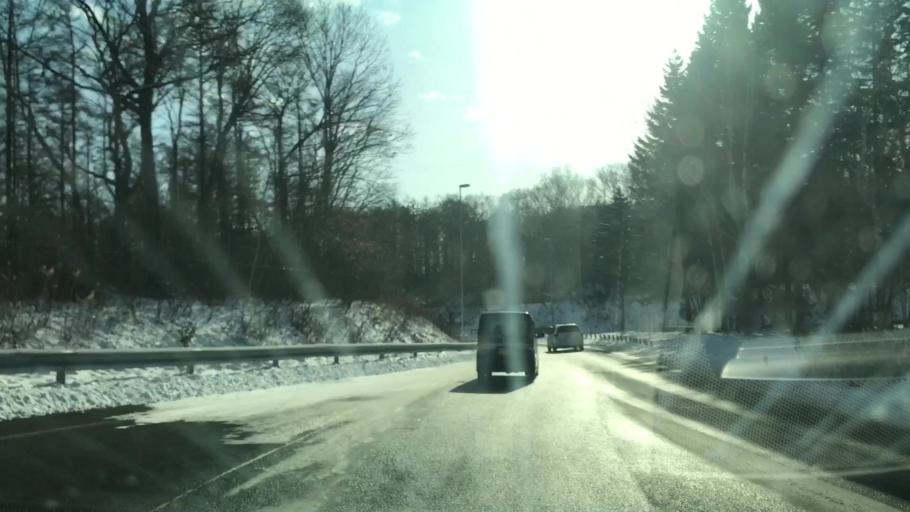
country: JP
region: Hokkaido
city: Chitose
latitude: 42.8116
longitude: 141.6262
